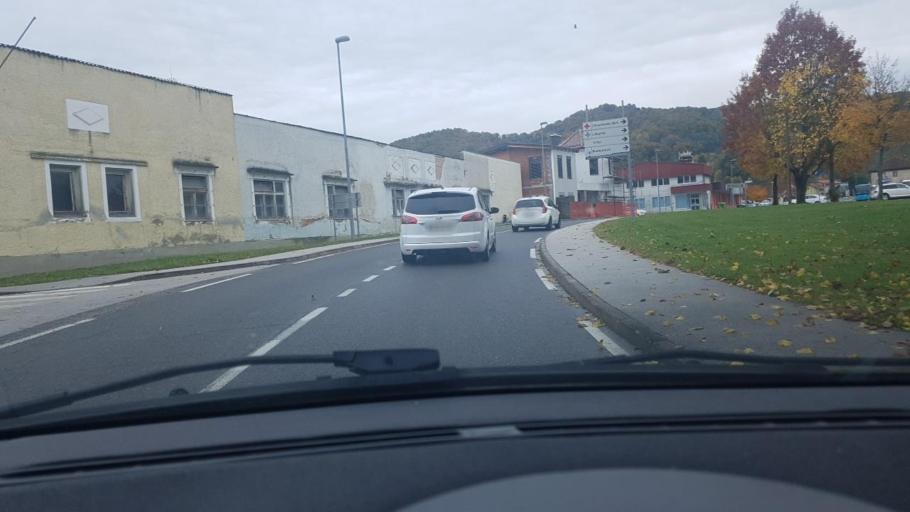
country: SI
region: Majsperk
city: Majsperk
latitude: 46.3401
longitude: 15.7365
